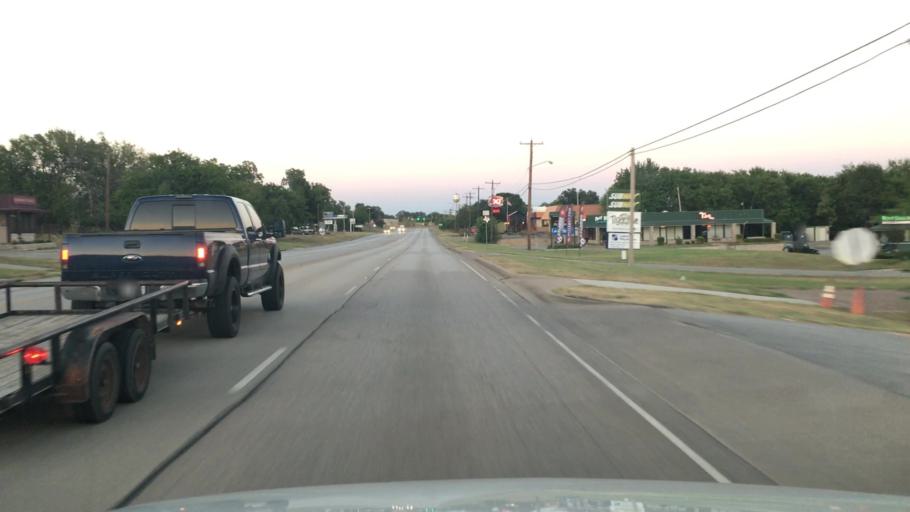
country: US
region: Texas
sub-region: Somervell County
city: Glen Rose
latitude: 32.2341
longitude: -97.7671
